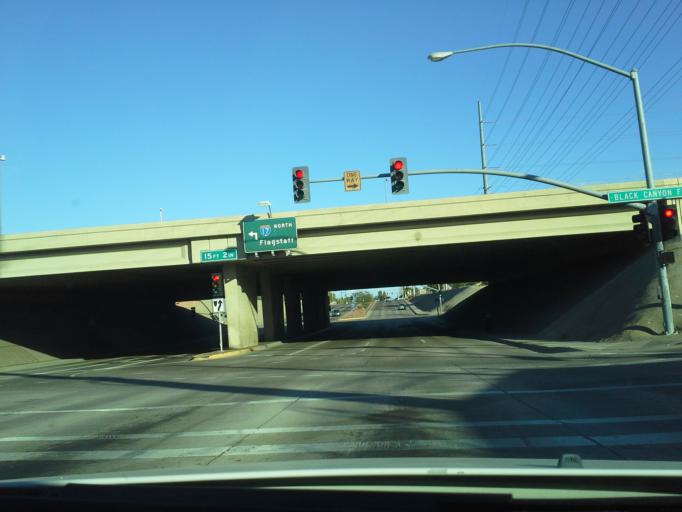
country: US
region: Arizona
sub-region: Maricopa County
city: Glendale
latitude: 33.6546
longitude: -112.1153
